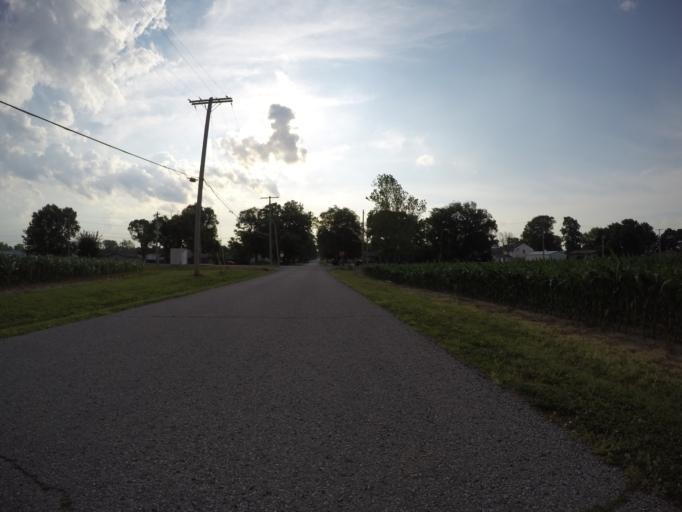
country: US
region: Kansas
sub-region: Doniphan County
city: Elwood
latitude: 39.7518
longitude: -94.8784
